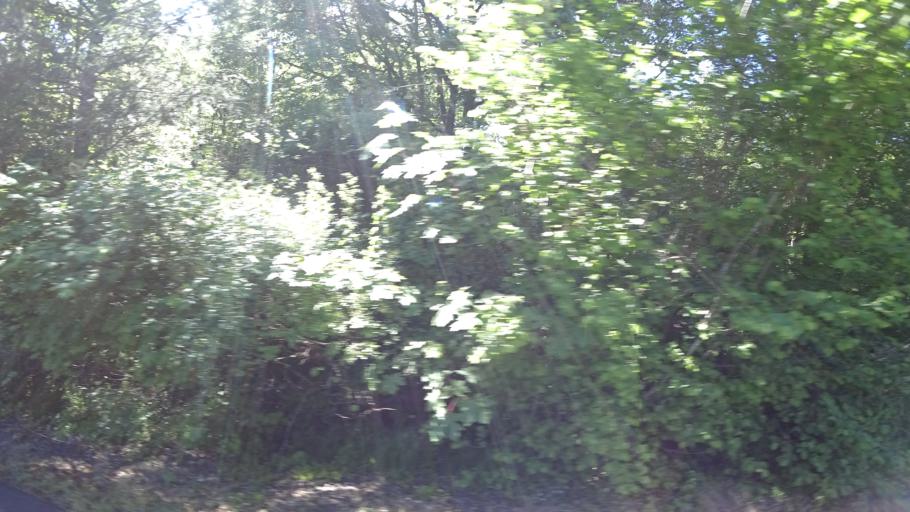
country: US
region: Oregon
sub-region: Washington County
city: Cedar Mill
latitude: 45.5518
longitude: -122.7980
